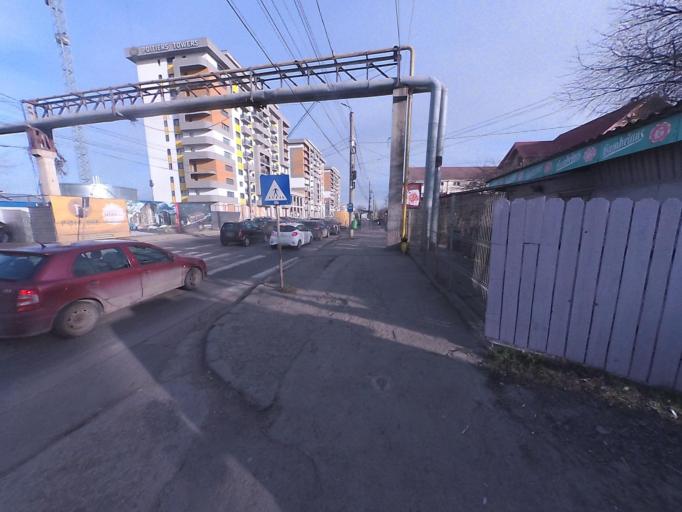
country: RO
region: Iasi
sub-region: Municipiul Iasi
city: Iasi
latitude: 47.1368
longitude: 27.6002
